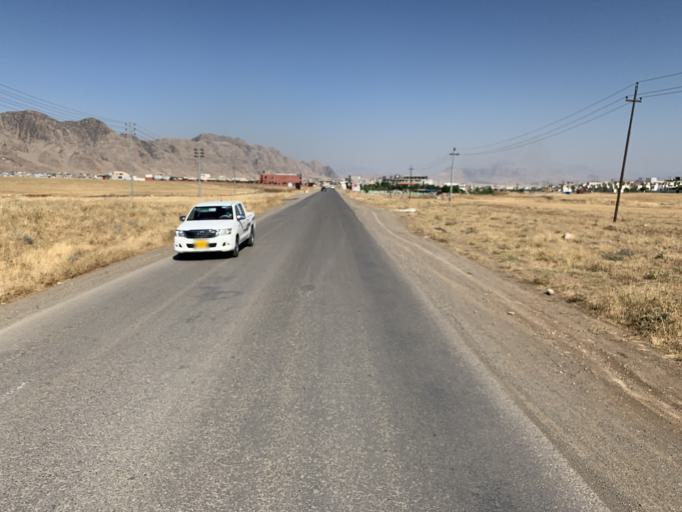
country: IQ
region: As Sulaymaniyah
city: Raniye
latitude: 36.2629
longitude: 44.8499
